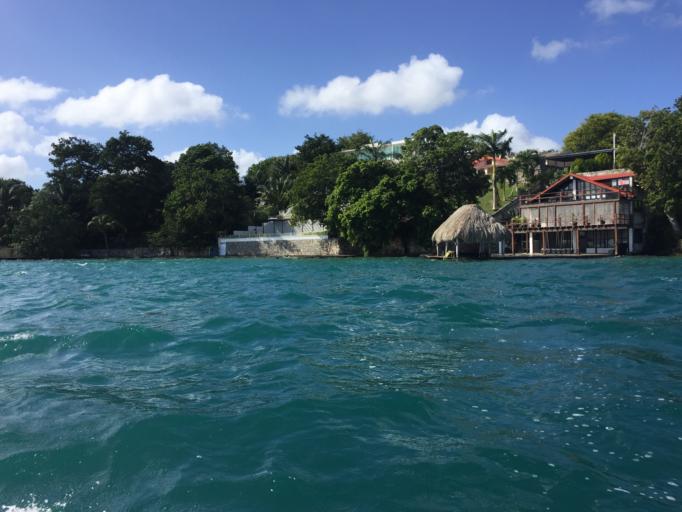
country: MX
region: Quintana Roo
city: Bacalar
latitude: 18.6564
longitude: -88.4054
